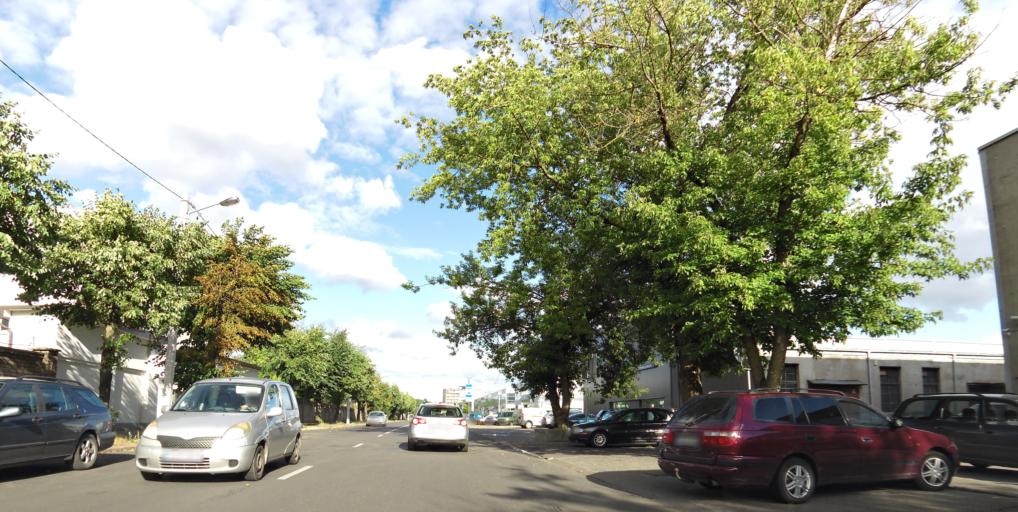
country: LT
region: Vilnius County
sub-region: Vilnius
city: Vilnius
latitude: 54.7149
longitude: 25.2991
